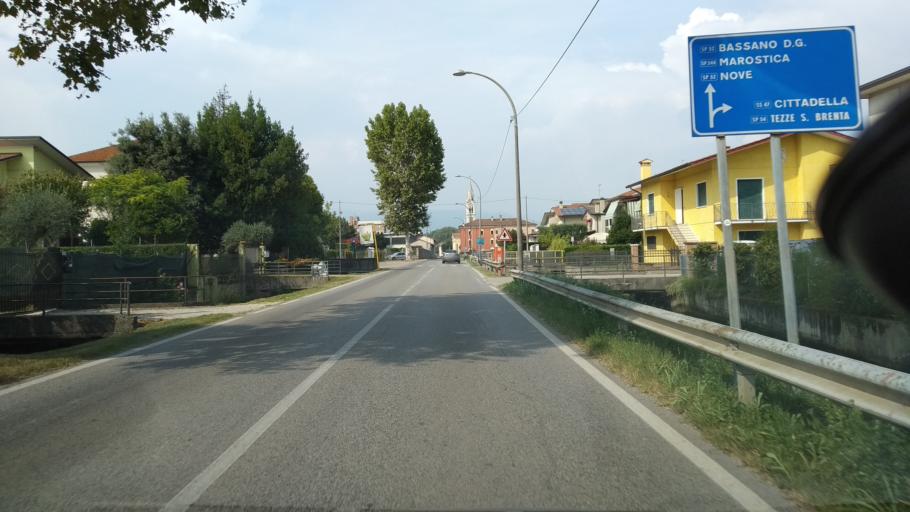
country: IT
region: Veneto
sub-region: Provincia di Vicenza
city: Pozzoleone
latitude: 45.6744
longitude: 11.6823
